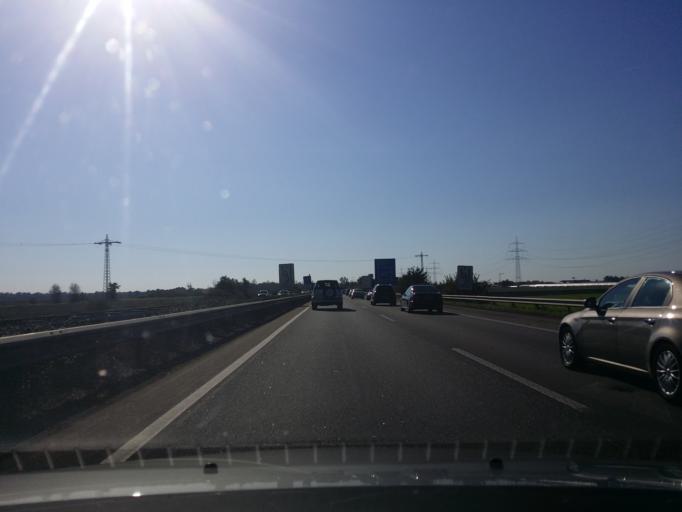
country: DE
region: Rheinland-Pfalz
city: Maxdorf
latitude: 49.4932
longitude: 8.3119
